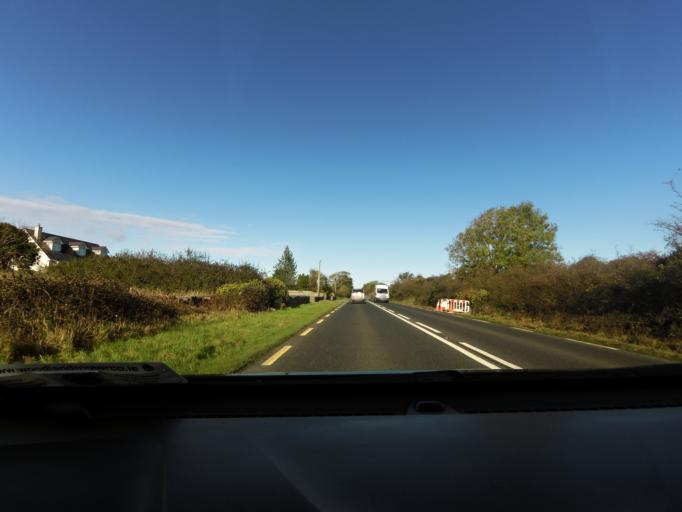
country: IE
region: Connaught
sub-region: County Galway
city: Claregalway
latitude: 53.4120
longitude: -9.0206
